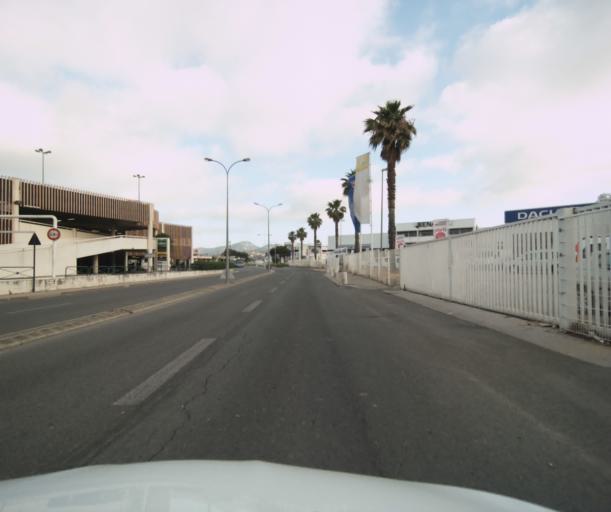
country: FR
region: Provence-Alpes-Cote d'Azur
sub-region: Departement du Var
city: Six-Fours-les-Plages
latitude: 43.1123
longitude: 5.8591
